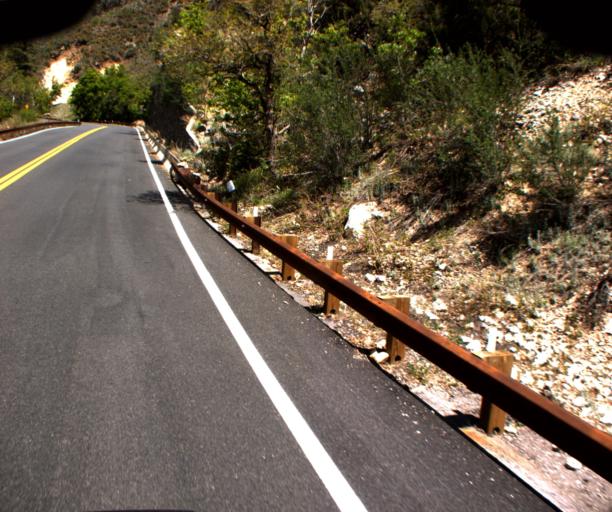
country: US
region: Arizona
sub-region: Coconino County
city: Kachina Village
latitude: 35.0271
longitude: -111.7416
